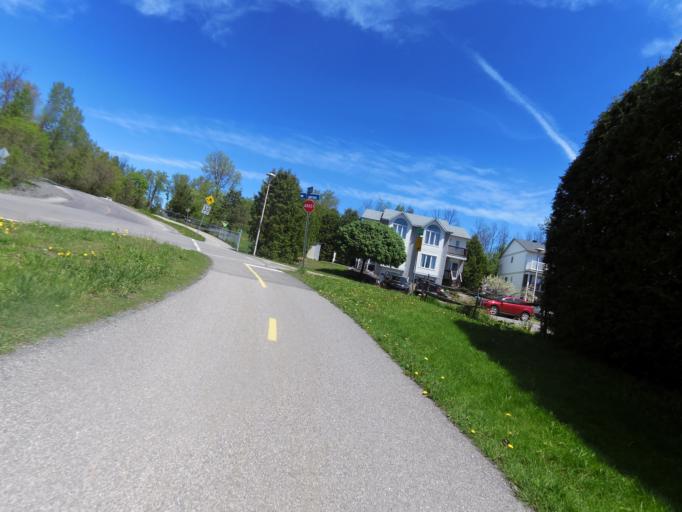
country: CA
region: Ontario
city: Bells Corners
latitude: 45.4054
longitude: -75.8724
